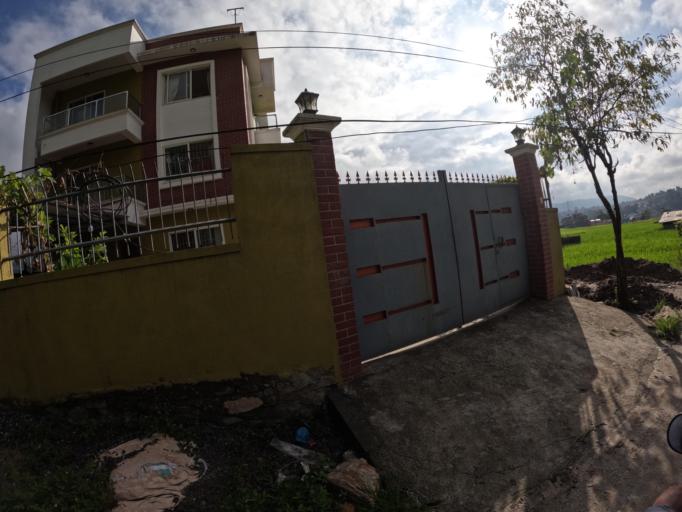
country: NP
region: Central Region
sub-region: Bagmati Zone
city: Kathmandu
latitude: 27.7658
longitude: 85.3333
